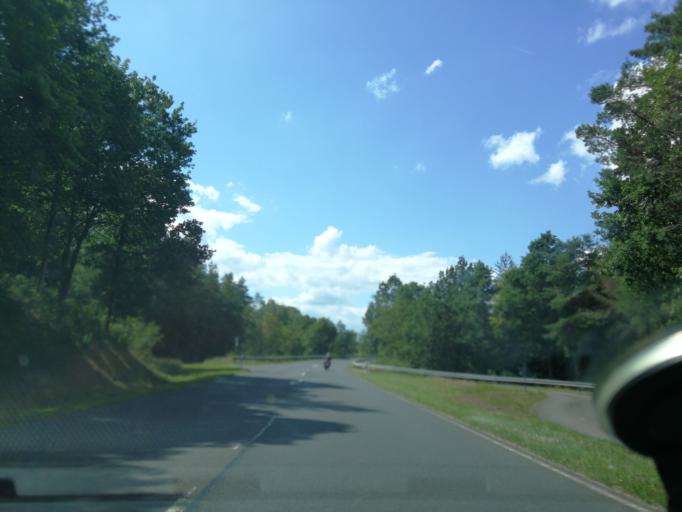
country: DE
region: Rheinland-Pfalz
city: Binsfeld
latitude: 49.9637
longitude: 6.7203
